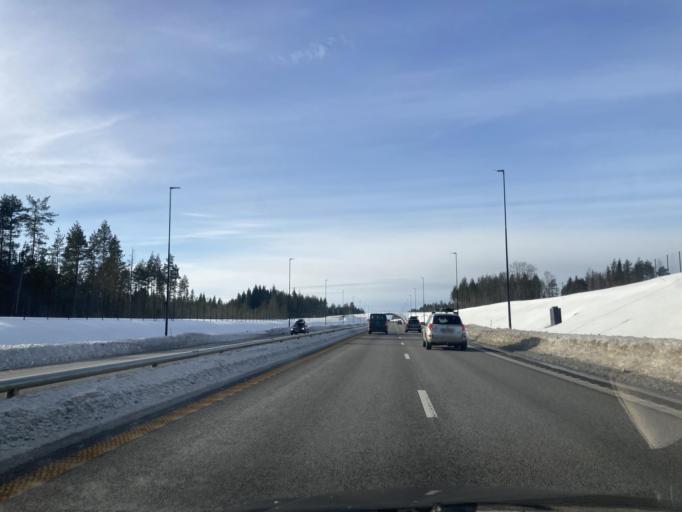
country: NO
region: Hedmark
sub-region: Loten
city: Loten
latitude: 60.8633
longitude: 11.4227
